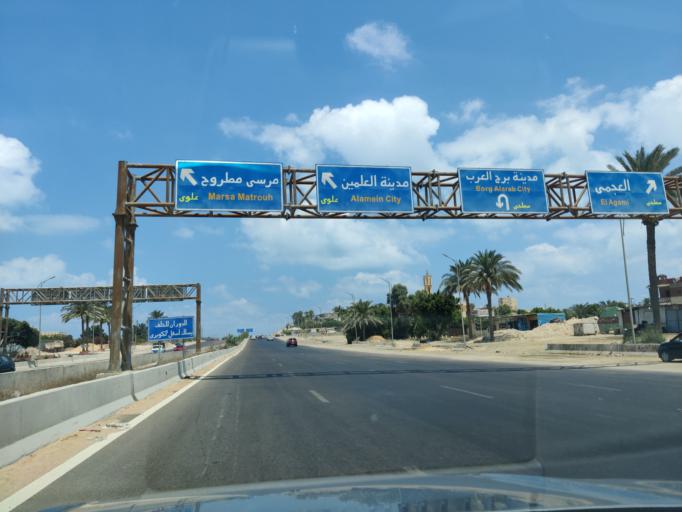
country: EG
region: Alexandria
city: Alexandria
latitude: 31.0083
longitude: 29.6380
